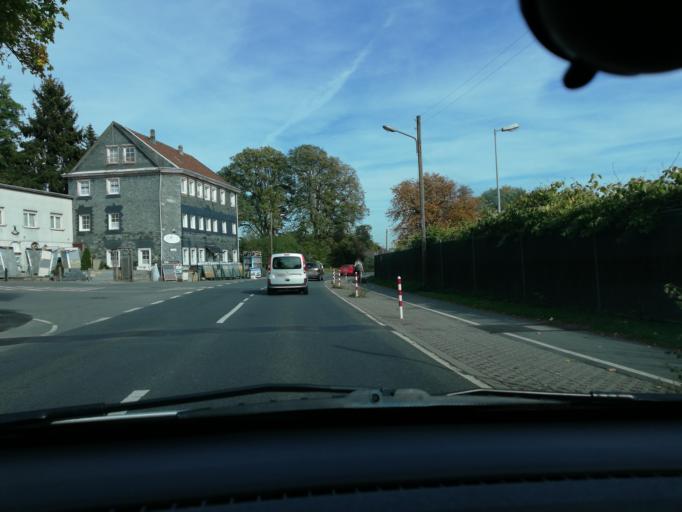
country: DE
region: North Rhine-Westphalia
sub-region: Regierungsbezirk Dusseldorf
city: Wuppertal
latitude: 51.2937
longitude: 7.1913
